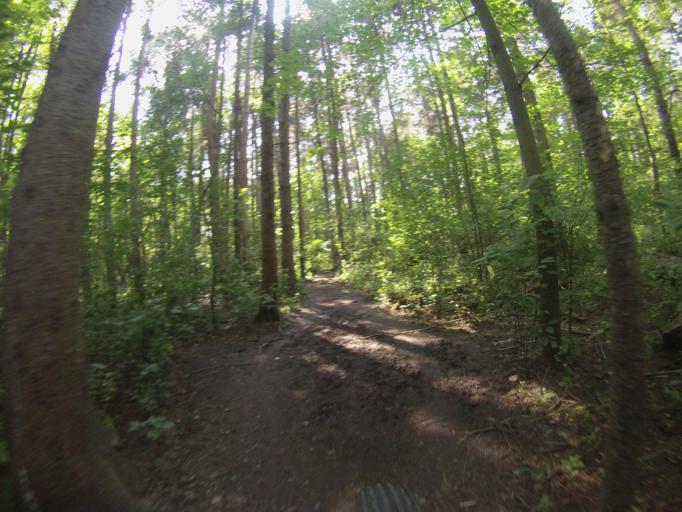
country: CA
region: Ontario
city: Ottawa
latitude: 45.3545
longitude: -75.6207
